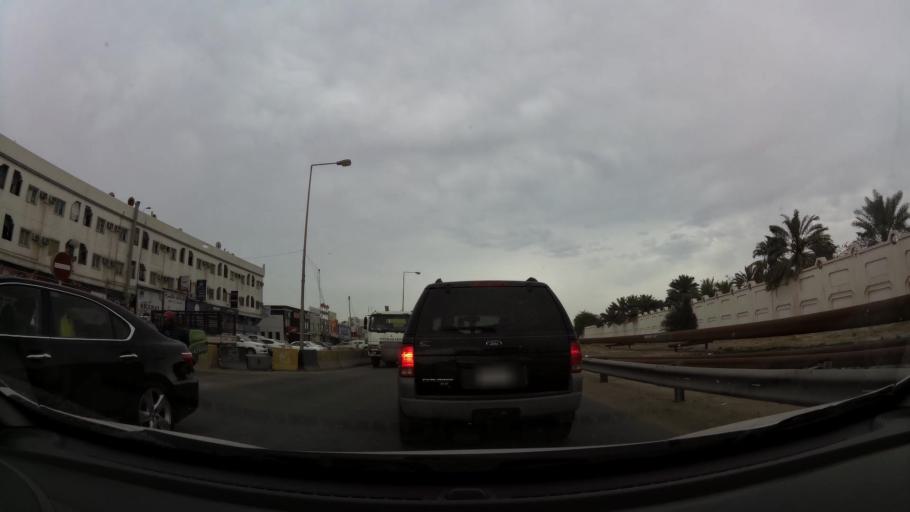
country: BH
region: Central Governorate
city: Madinat Hamad
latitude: 26.1456
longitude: 50.4913
